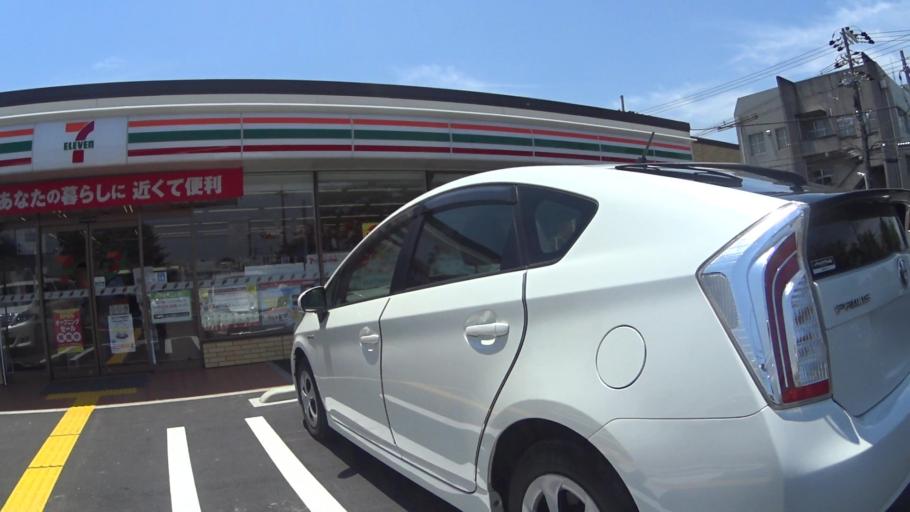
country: JP
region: Kyoto
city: Ayabe
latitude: 35.2624
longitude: 135.1893
